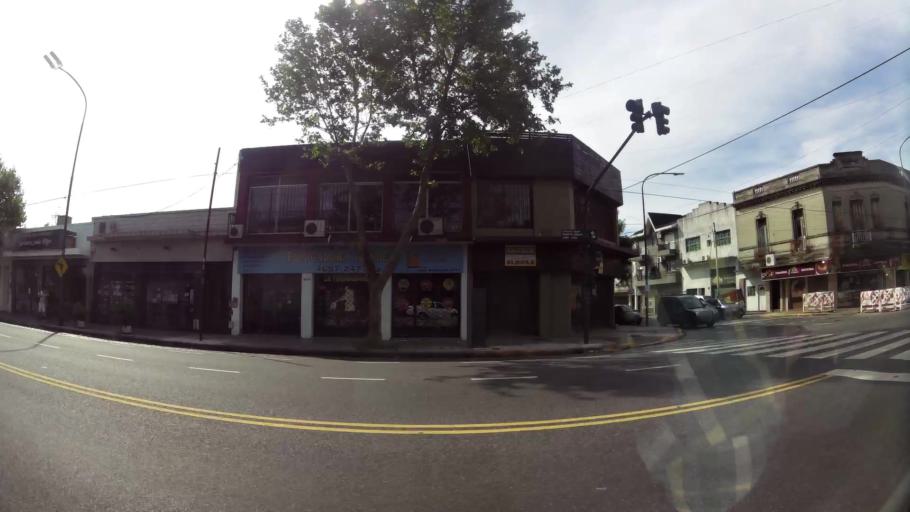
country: AR
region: Buenos Aires F.D.
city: Villa Lugano
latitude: -34.6572
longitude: -58.5098
